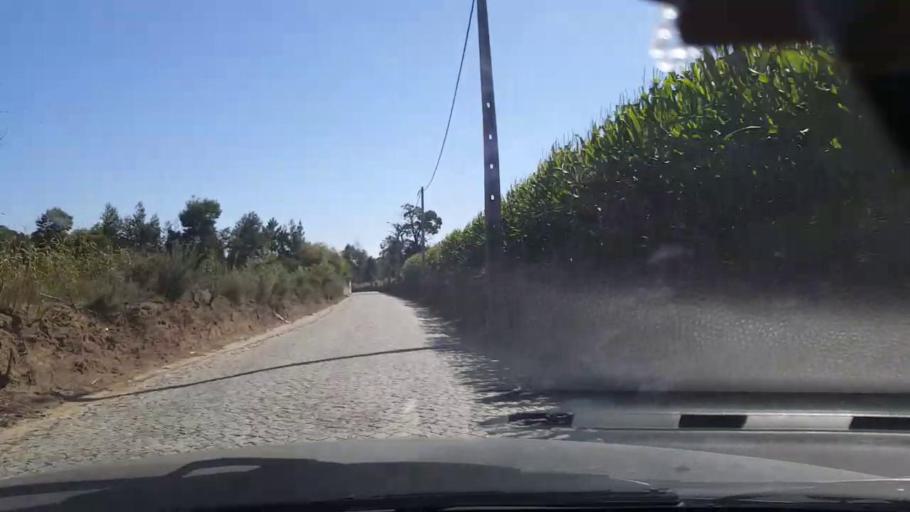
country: PT
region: Porto
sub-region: Vila do Conde
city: Arvore
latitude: 41.3143
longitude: -8.6875
